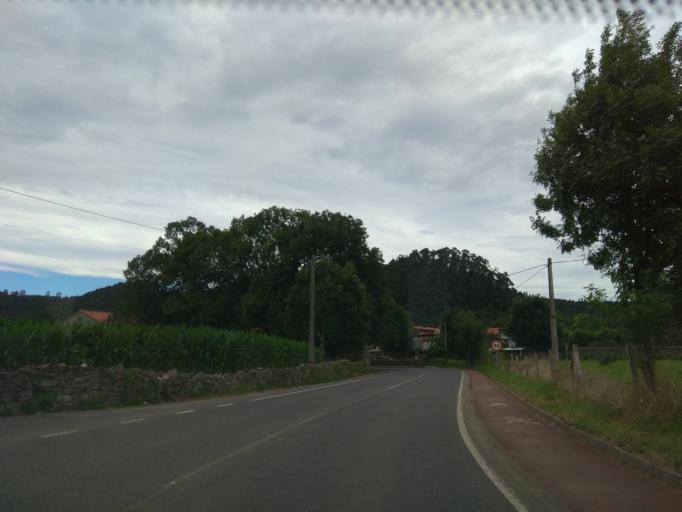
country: ES
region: Cantabria
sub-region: Provincia de Cantabria
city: Hazas de Cesto
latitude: 43.3982
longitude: -3.5970
